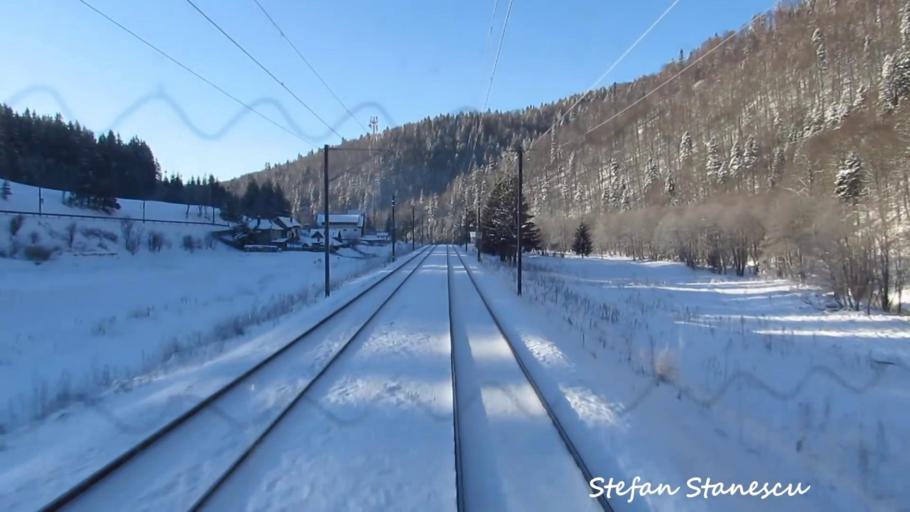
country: RO
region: Prahova
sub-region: Oras Azuga
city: Azuga
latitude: 45.4679
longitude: 25.5597
